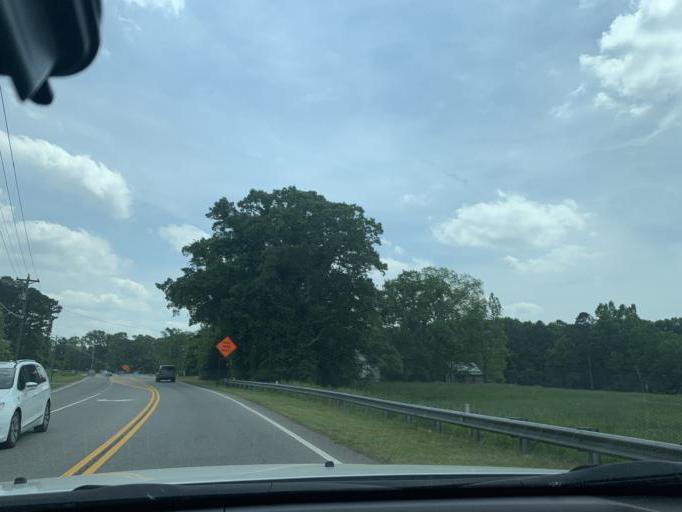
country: US
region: Georgia
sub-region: Forsyth County
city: Cumming
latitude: 34.1508
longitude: -84.1517
